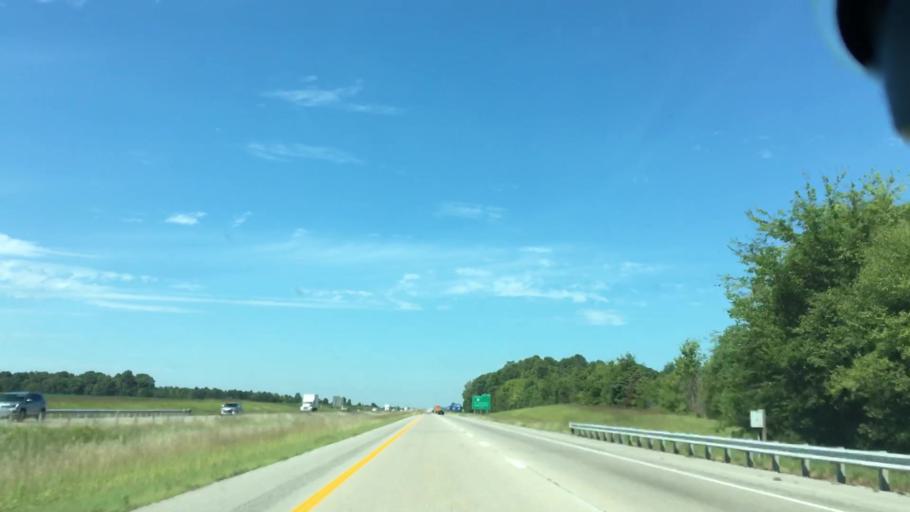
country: US
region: Kentucky
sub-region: Christian County
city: Oak Grove
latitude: 36.6941
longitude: -87.4304
